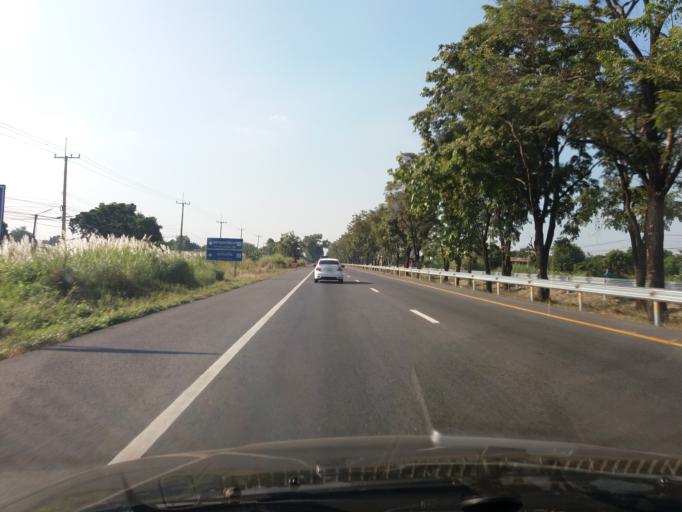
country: TH
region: Nakhon Sawan
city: Banphot Phisai
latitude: 15.8049
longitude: 99.9528
